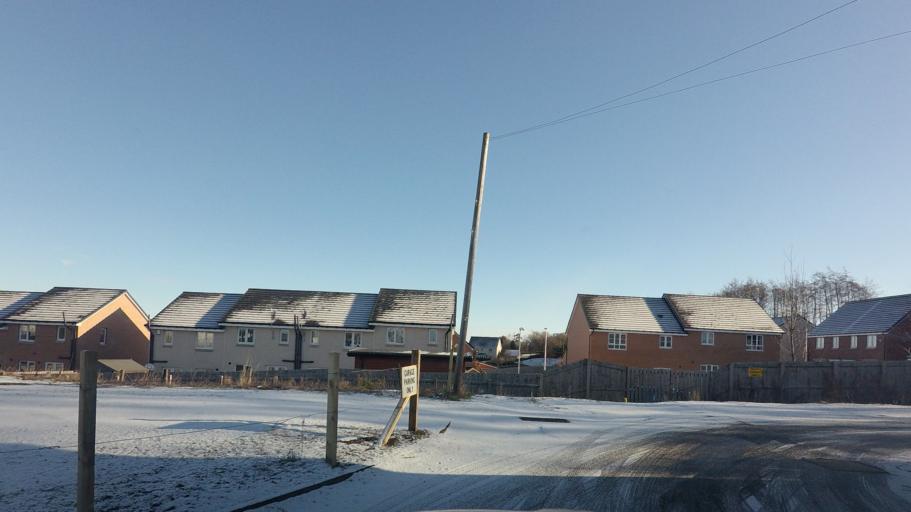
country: GB
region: Scotland
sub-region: Fife
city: Aberdour
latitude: 56.0453
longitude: -3.3436
